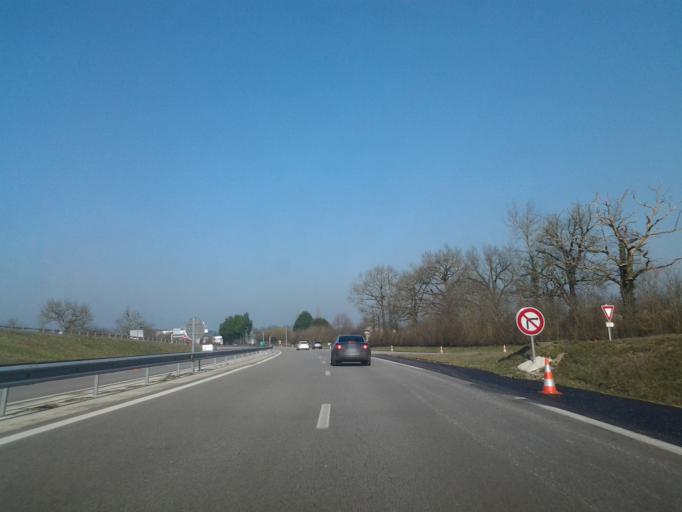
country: FR
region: Pays de la Loire
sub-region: Departement de la Vendee
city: Aizenay
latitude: 46.7471
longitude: -1.6231
